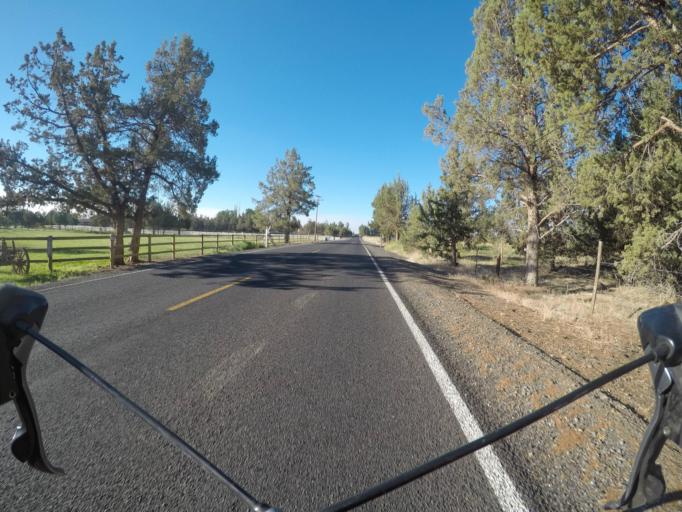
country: US
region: Oregon
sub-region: Deschutes County
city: Redmond
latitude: 44.2591
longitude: -121.2396
